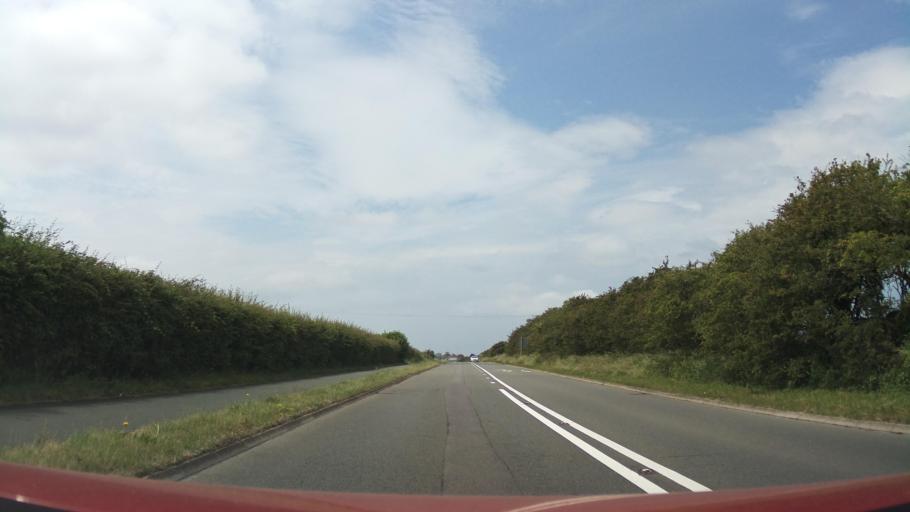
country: GB
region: Wales
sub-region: Vale of Glamorgan
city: Rhoose
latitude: 51.3899
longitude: -3.3289
